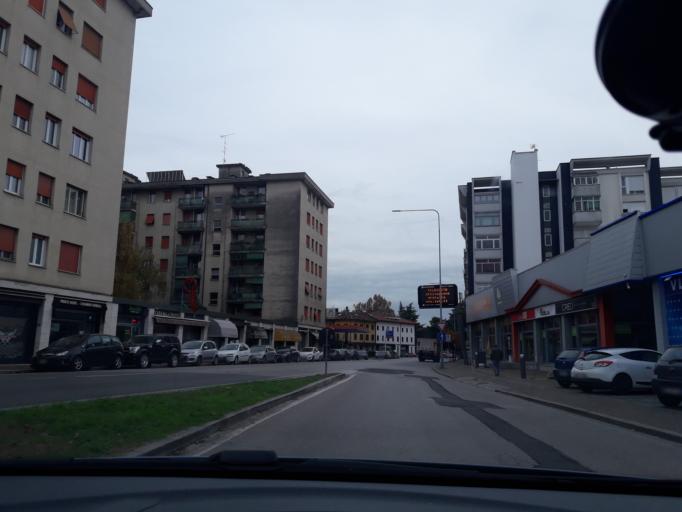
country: IT
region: Friuli Venezia Giulia
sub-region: Provincia di Udine
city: Udine
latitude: 46.0800
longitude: 13.2341
